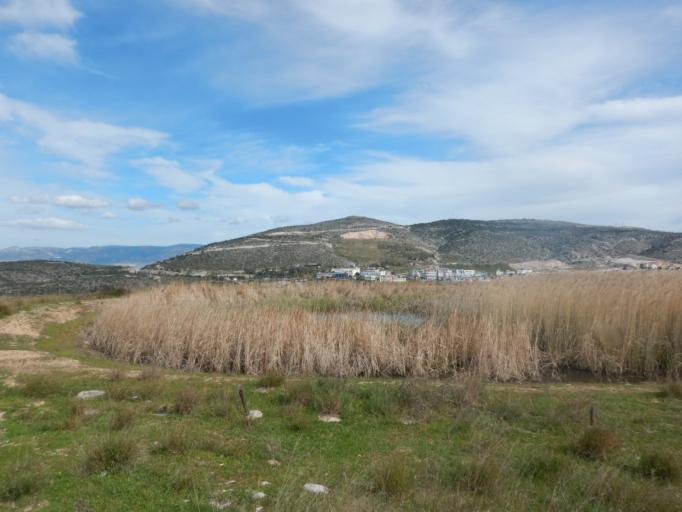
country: GR
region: Attica
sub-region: Nomos Piraios
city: Perama
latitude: 37.9740
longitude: 23.5902
